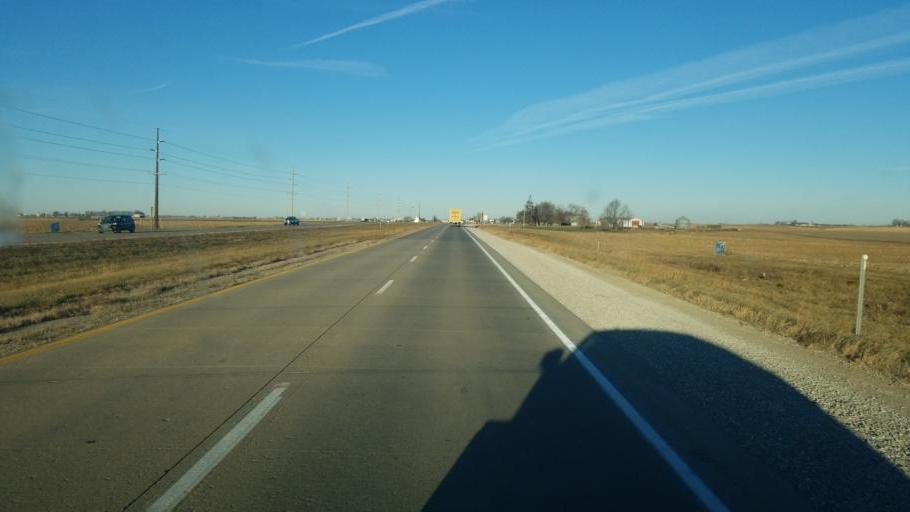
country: US
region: Iowa
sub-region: Marion County
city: Pella
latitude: 41.3644
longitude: -92.7863
